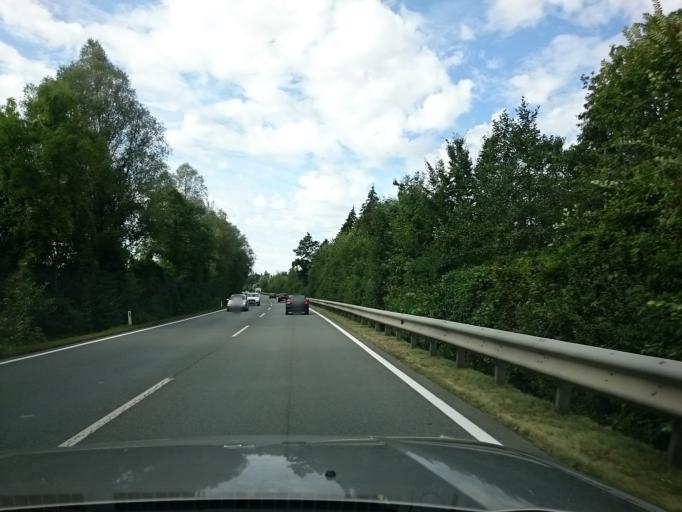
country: DE
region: Bavaria
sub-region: Upper Bavaria
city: Laufen
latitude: 47.9191
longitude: 12.9740
